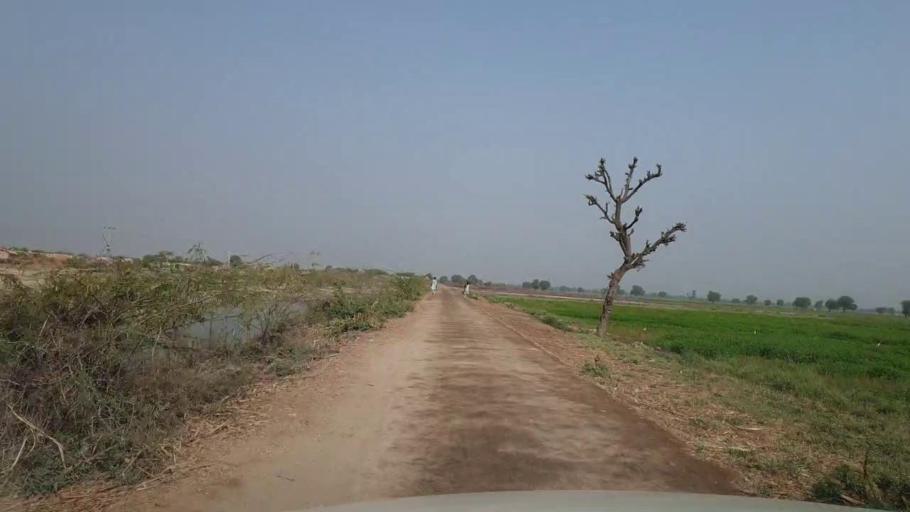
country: PK
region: Sindh
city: Umarkot
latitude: 25.4281
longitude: 69.7070
